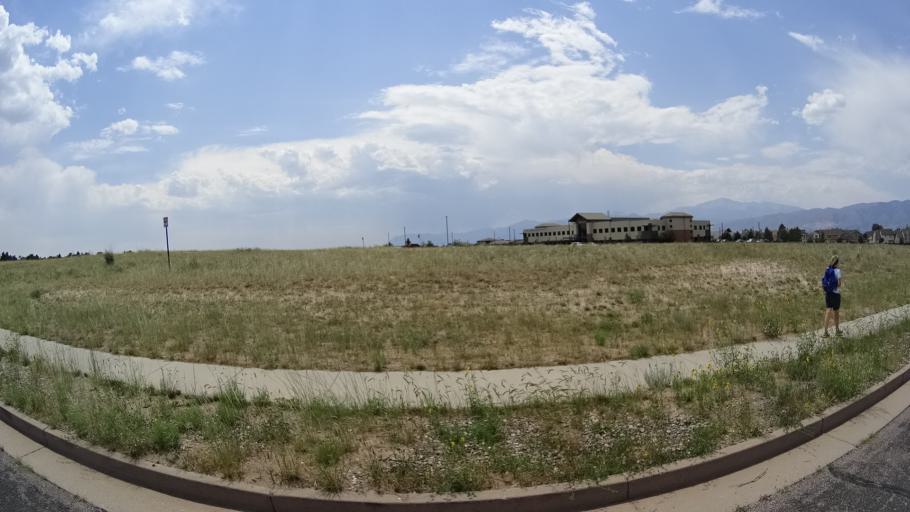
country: US
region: Colorado
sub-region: El Paso County
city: Black Forest
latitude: 38.9618
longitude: -104.7643
